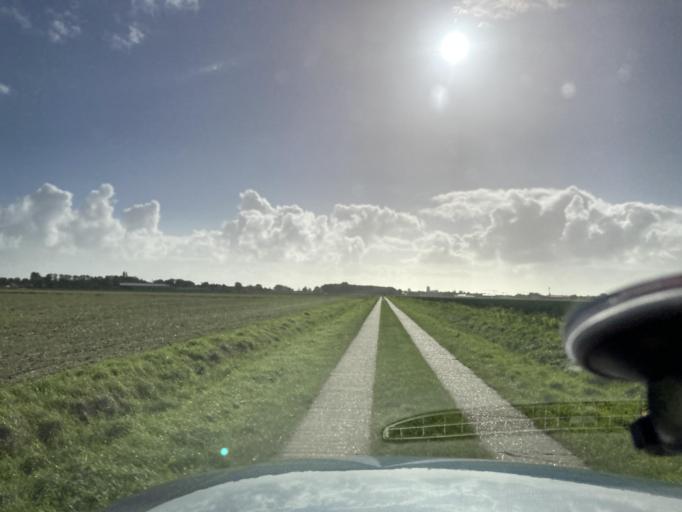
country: DE
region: Schleswig-Holstein
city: Oesterdeichstrich
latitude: 54.1456
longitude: 8.8932
